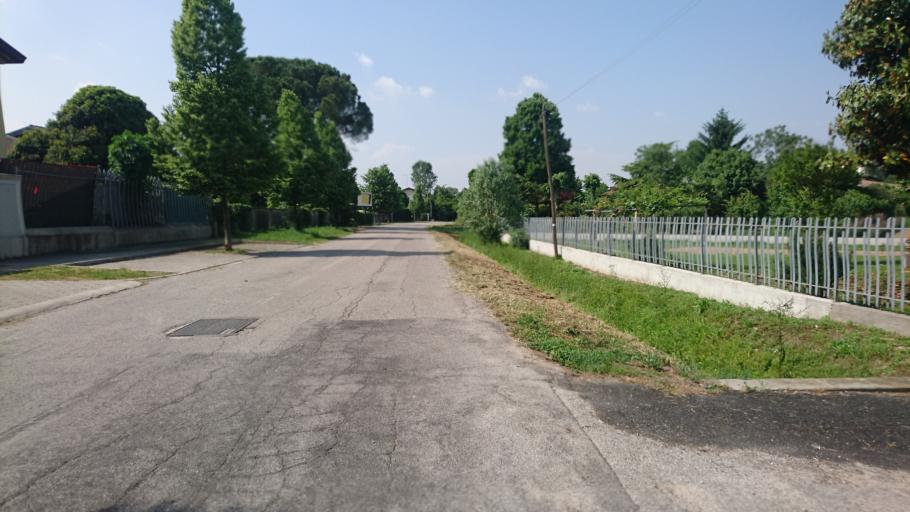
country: IT
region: Veneto
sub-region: Provincia di Venezia
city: Vigonovo
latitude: 45.3919
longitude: 12.0045
